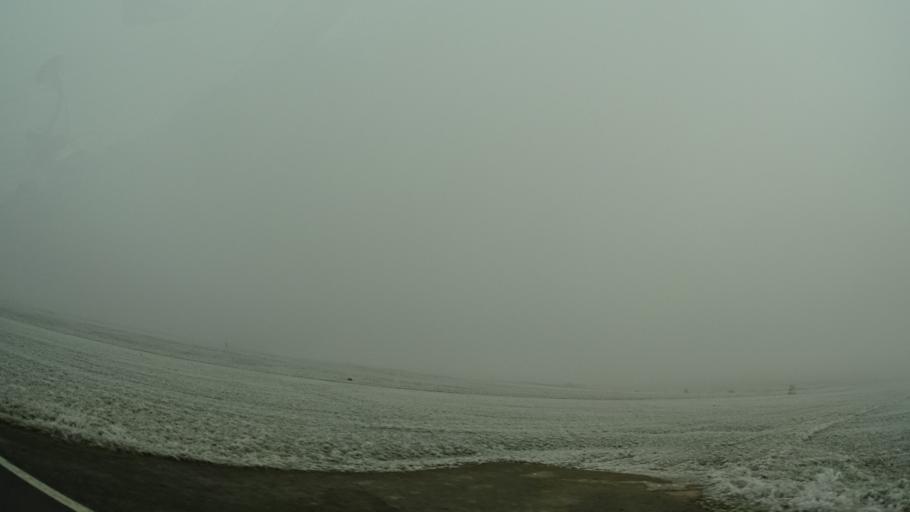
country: DE
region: Thuringia
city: Henneberg
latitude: 50.5159
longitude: 10.3131
